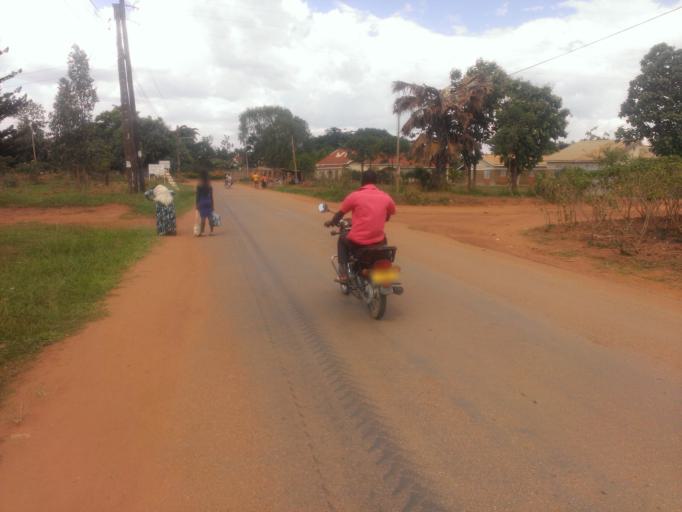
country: UG
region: Northern Region
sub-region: Gulu District
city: Gulu
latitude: 2.7828
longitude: 32.3022
